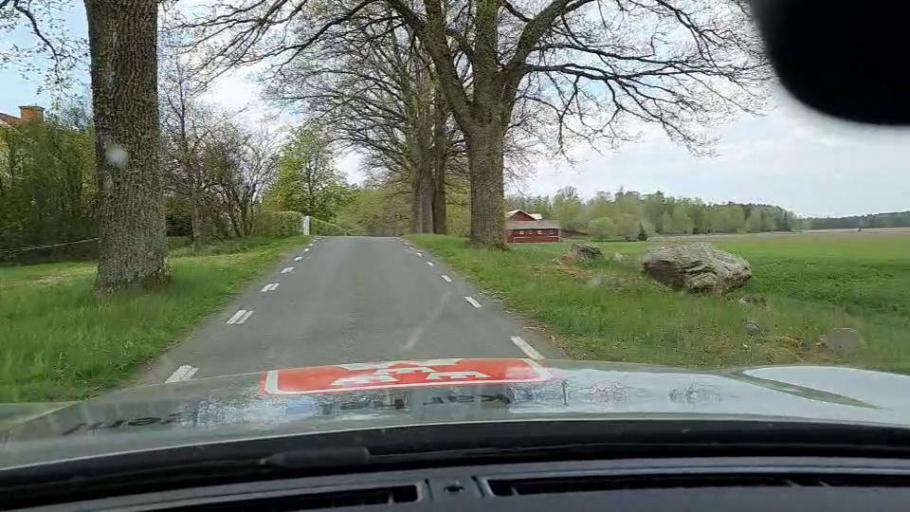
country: SE
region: Soedermanland
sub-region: Katrineholms Kommun
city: Katrineholm
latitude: 59.1770
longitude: 16.1081
